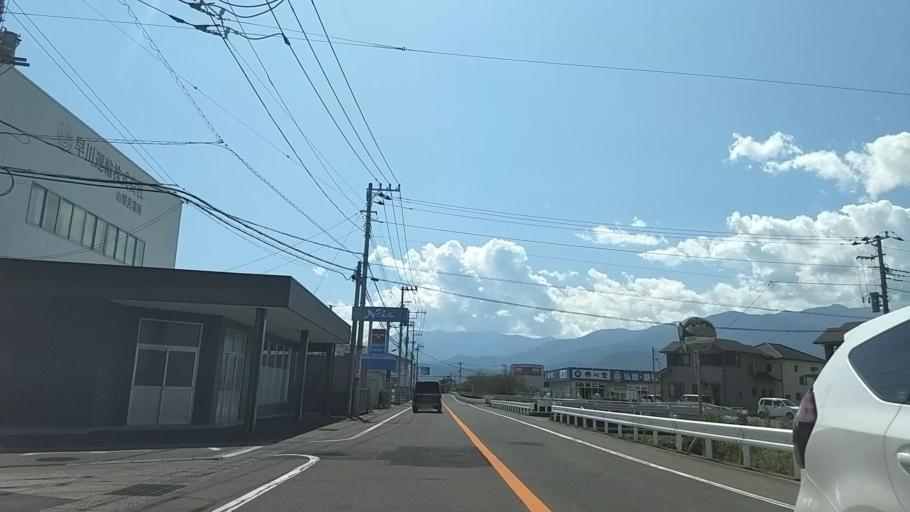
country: JP
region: Yamanashi
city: Ryuo
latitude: 35.5904
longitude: 138.5002
